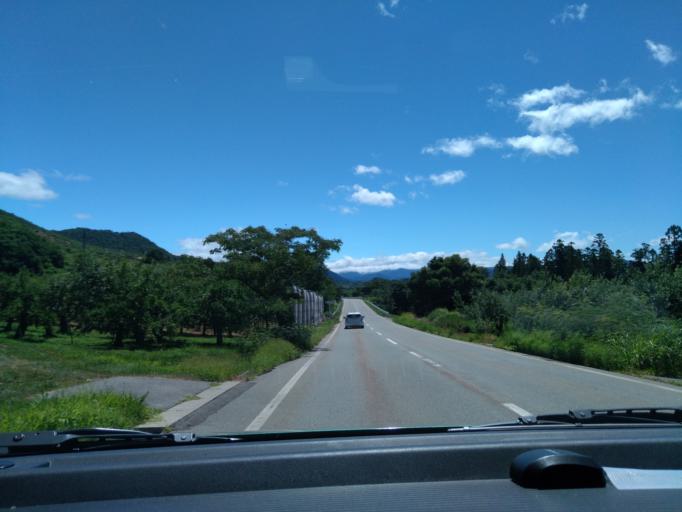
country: JP
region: Akita
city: Yuzawa
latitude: 39.2240
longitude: 140.5653
